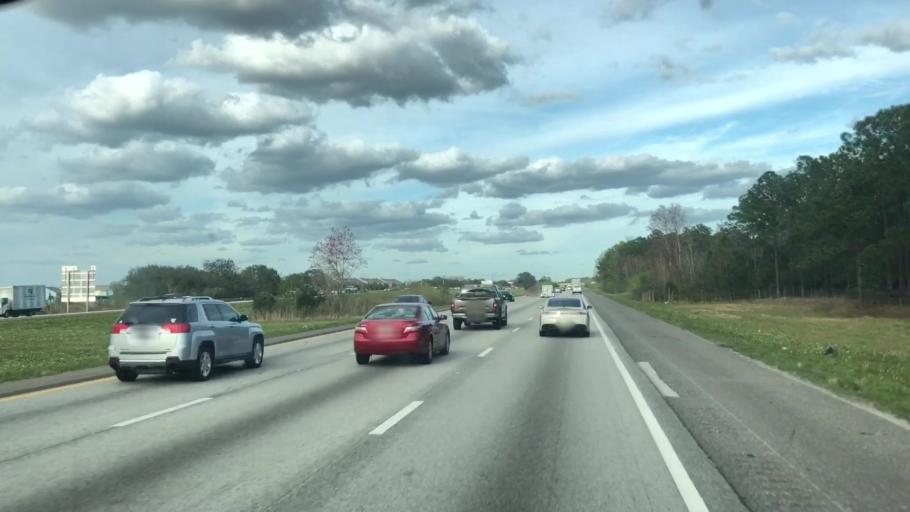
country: US
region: Florida
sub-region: Polk County
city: Loughman
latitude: 28.2438
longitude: -81.6340
